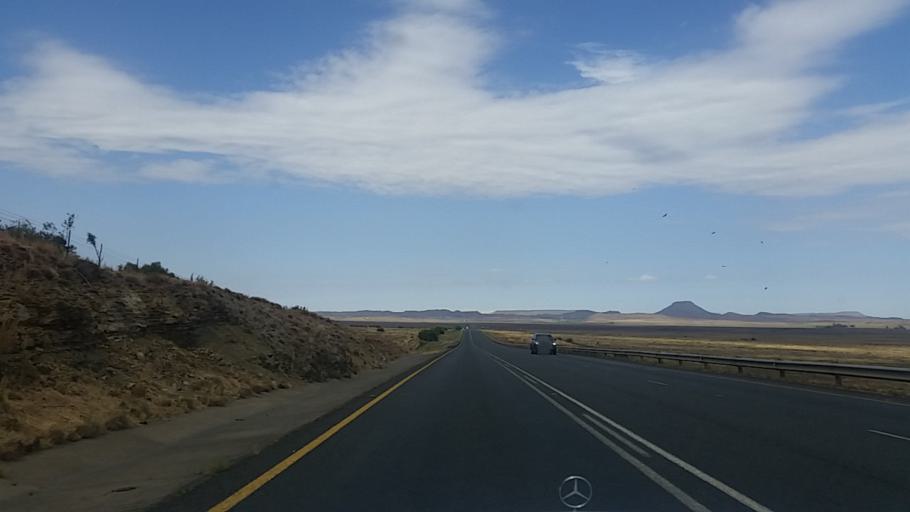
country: ZA
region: Northern Cape
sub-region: Pixley ka Seme District Municipality
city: Colesberg
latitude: -30.6523
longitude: 25.2005
